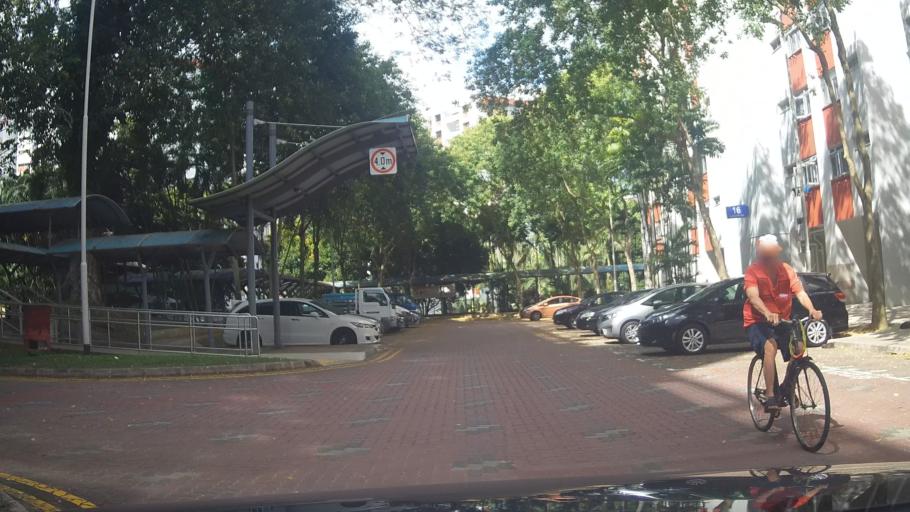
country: MY
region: Johor
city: Johor Bahru
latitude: 1.4416
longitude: 103.7780
